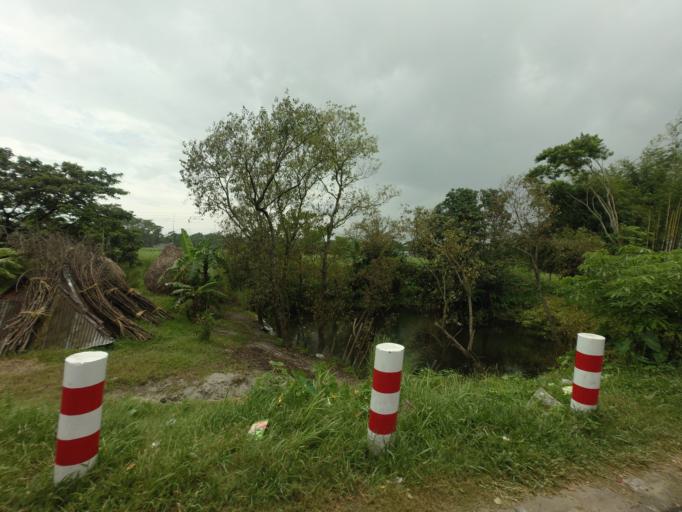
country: BD
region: Dhaka
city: Char Bhadrasan
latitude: 23.4107
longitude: 90.2153
